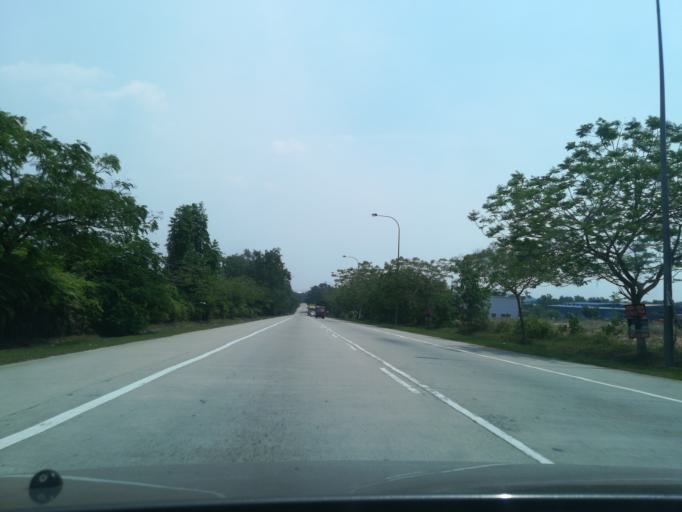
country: MY
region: Kedah
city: Kulim
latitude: 5.4178
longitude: 100.5668
